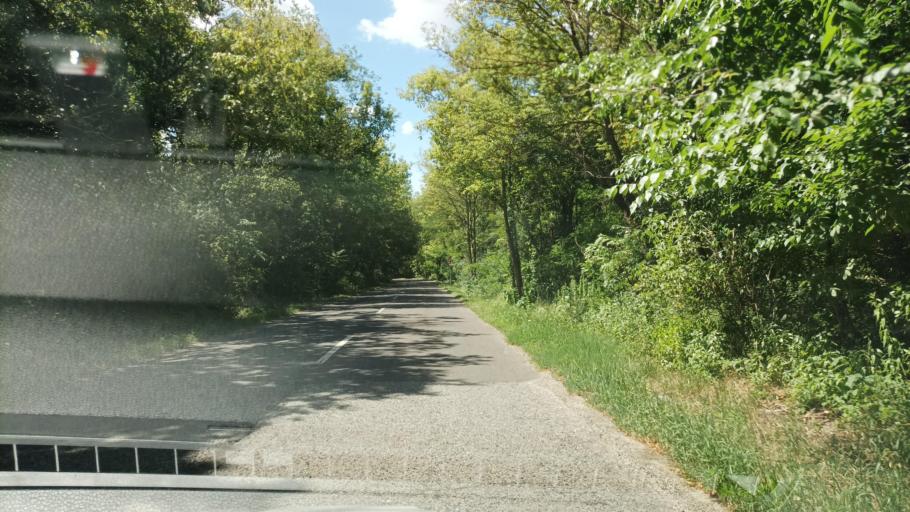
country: HU
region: Pest
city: Szentendre
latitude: 47.6736
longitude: 19.0885
